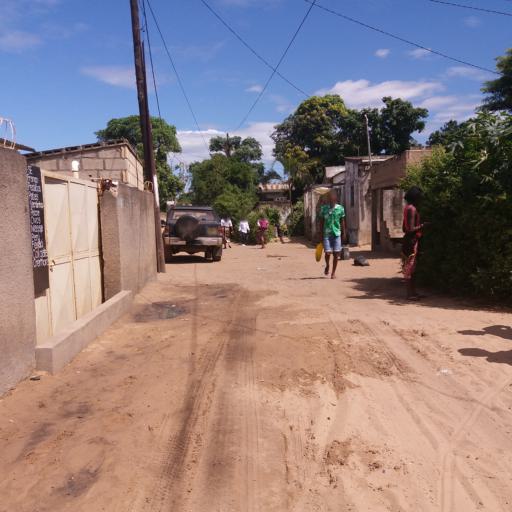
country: MZ
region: Maputo City
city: Maputo
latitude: -25.9045
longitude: 32.5920
